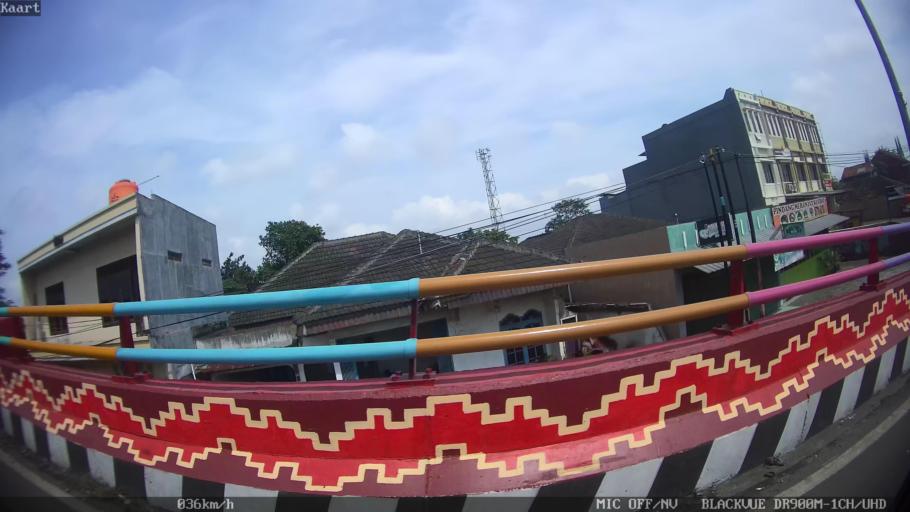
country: ID
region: Lampung
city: Kedaton
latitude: -5.3707
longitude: 105.2744
